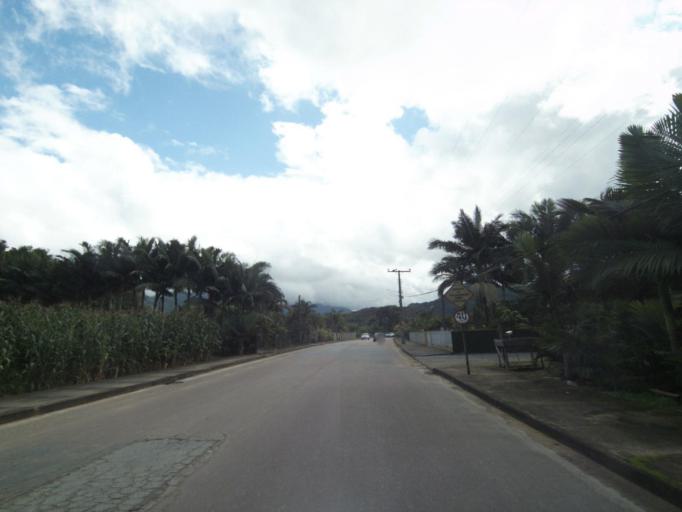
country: BR
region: Santa Catarina
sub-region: Pomerode
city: Pomerode
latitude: -26.6865
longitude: -49.1756
